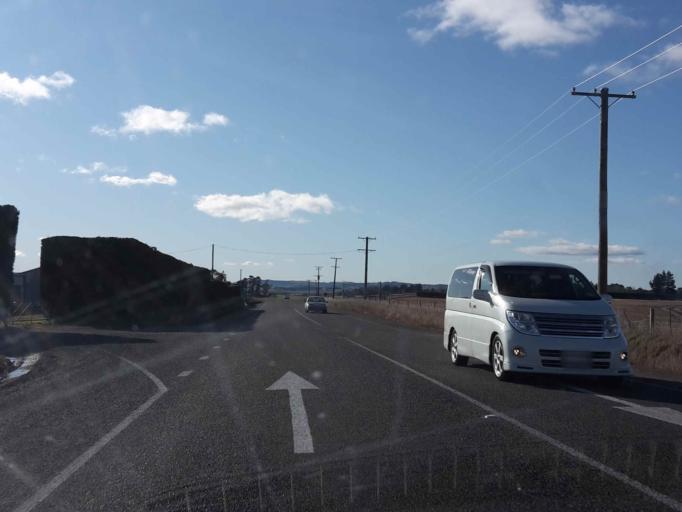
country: NZ
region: Otago
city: Oamaru
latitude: -45.2103
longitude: 170.8032
